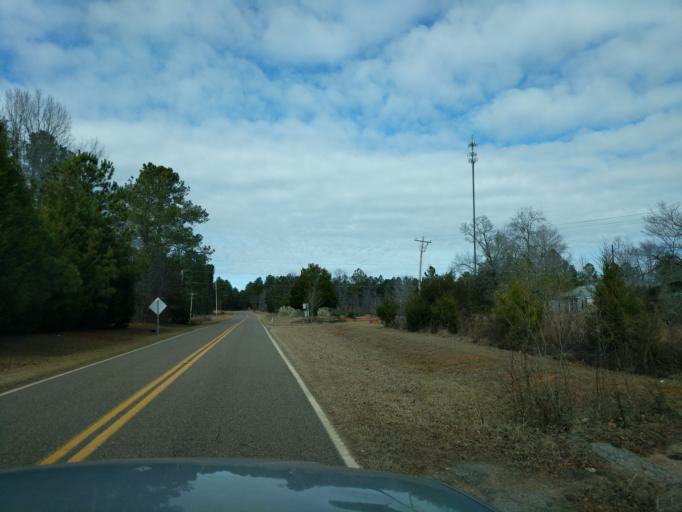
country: US
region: South Carolina
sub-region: Edgefield County
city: Edgefield
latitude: 33.8722
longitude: -81.9957
